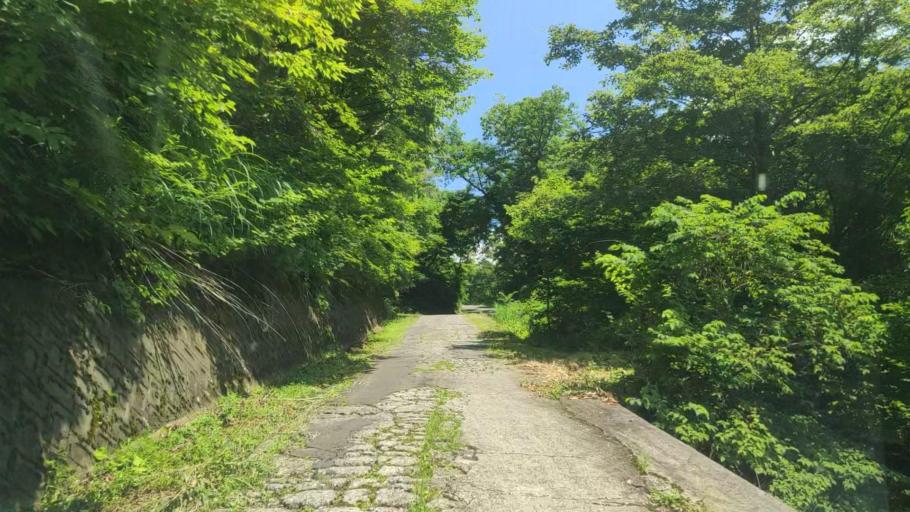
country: JP
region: Fukui
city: Ono
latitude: 35.7873
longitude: 136.5072
